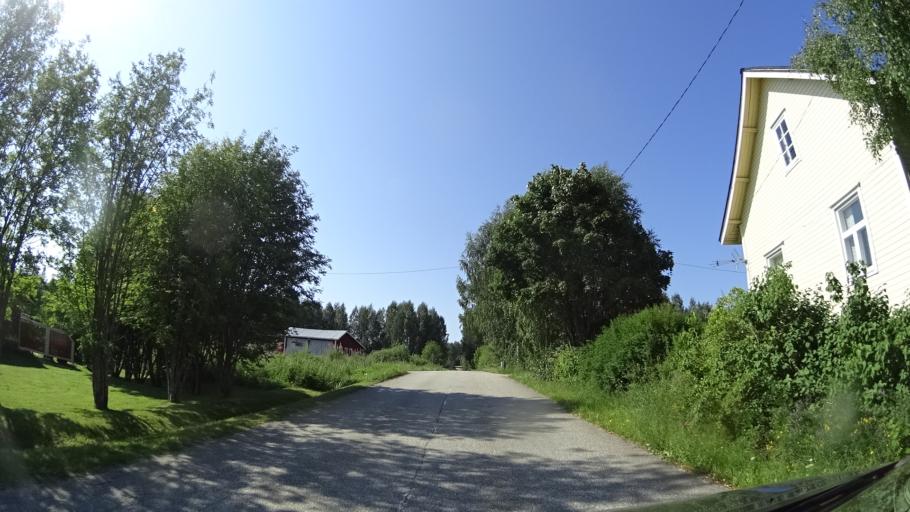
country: FI
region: North Karelia
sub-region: Joensuu
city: Juuka
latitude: 63.2389
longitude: 29.2468
